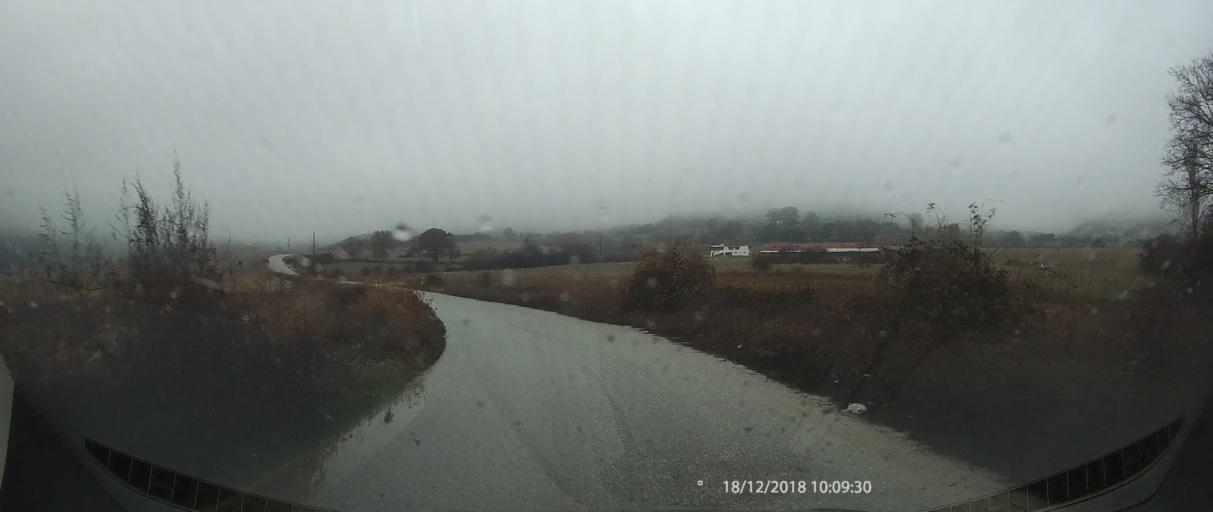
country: GR
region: Thessaly
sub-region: Nomos Larisis
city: Livadi
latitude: 40.0817
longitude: 22.2152
